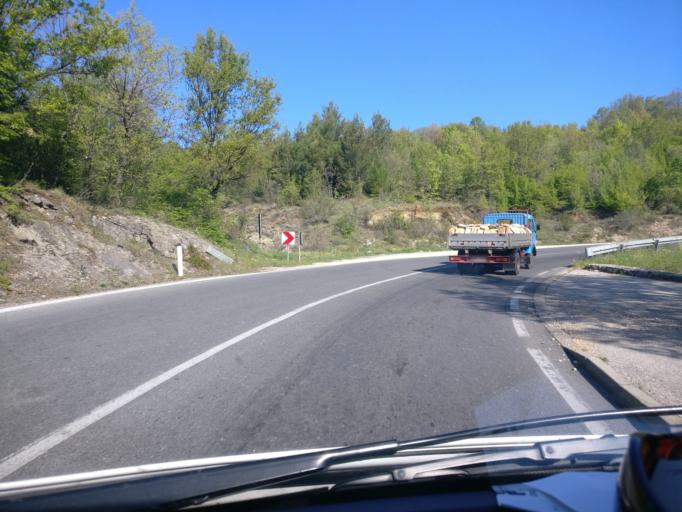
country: BA
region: Federation of Bosnia and Herzegovina
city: Crnici
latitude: 43.1027
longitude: 17.9040
